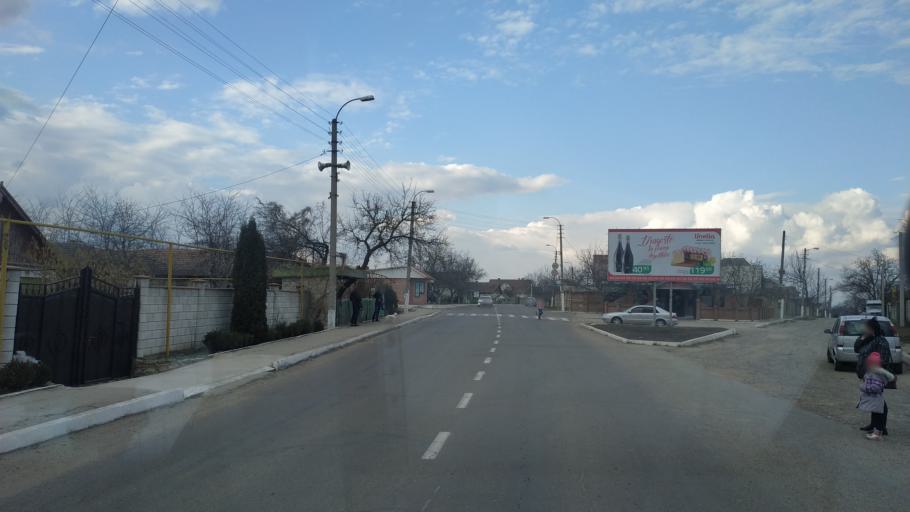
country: MD
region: Anenii Noi
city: Varnita
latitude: 46.8550
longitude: 29.4799
